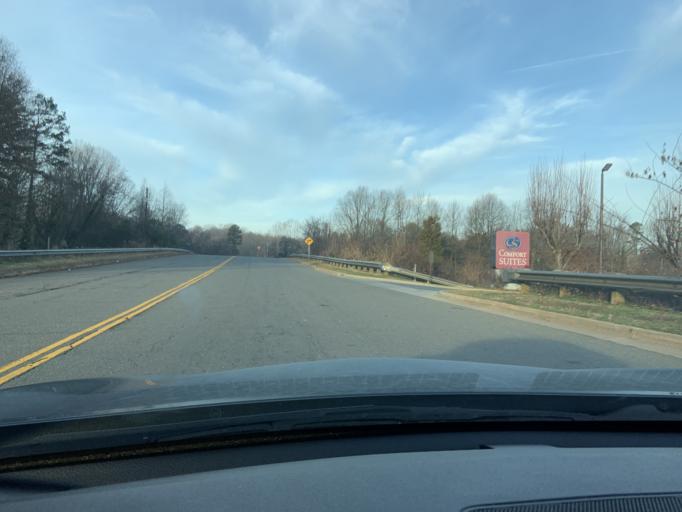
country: US
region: North Carolina
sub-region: Mecklenburg County
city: Charlotte
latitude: 35.2347
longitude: -80.9193
